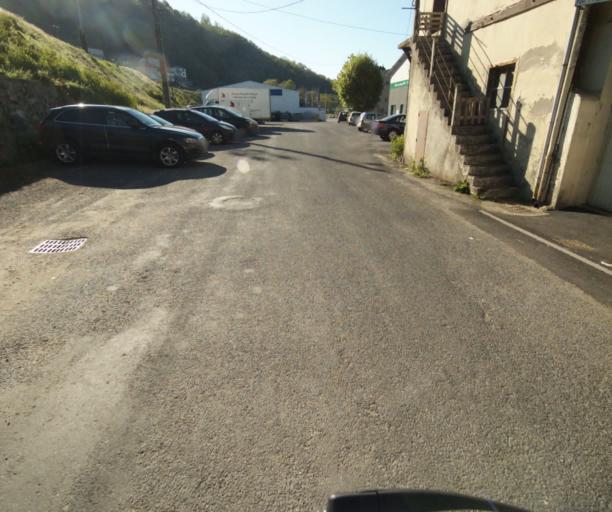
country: FR
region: Limousin
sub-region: Departement de la Correze
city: Tulle
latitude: 45.2566
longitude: 1.7590
